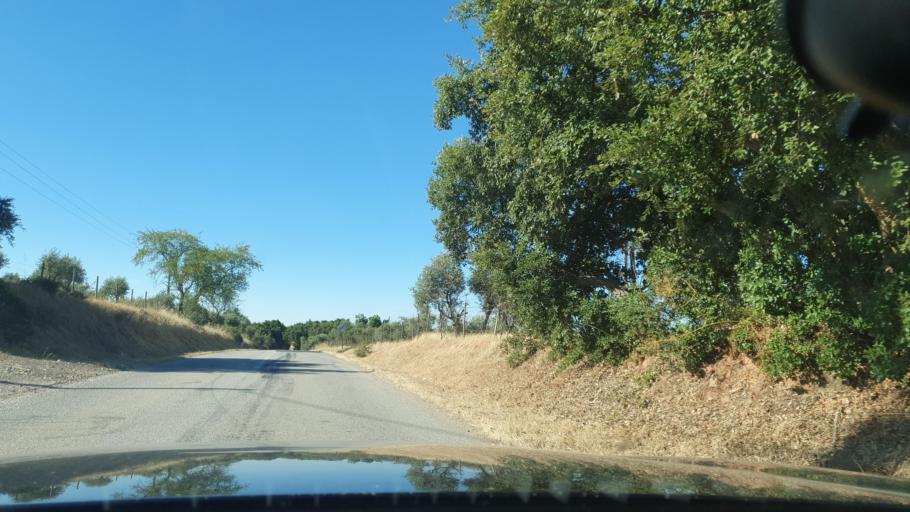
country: PT
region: Evora
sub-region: Alandroal
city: Alandroal
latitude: 38.7120
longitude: -7.4064
